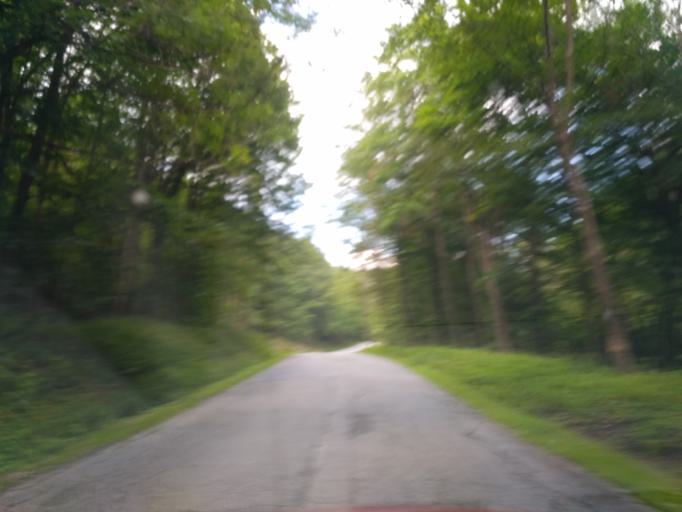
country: SK
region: Kosicky
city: Gelnica
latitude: 48.9191
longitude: 21.0357
